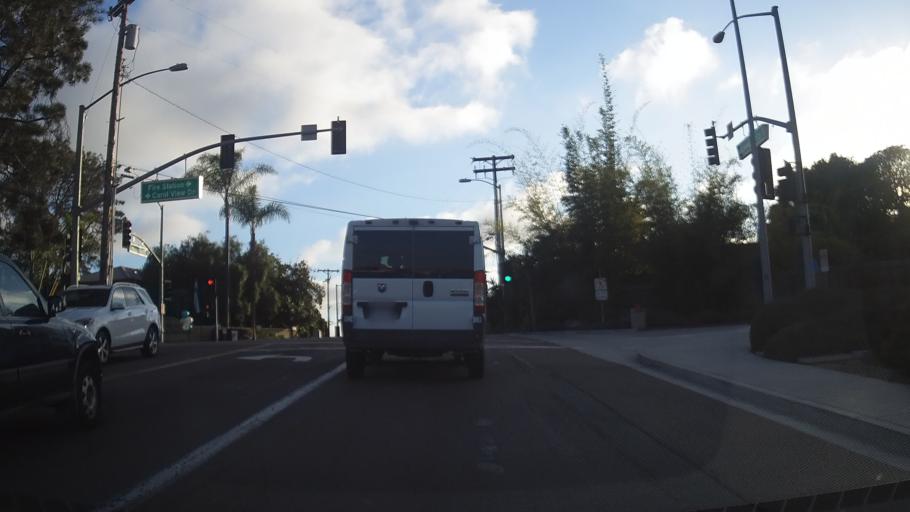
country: US
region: California
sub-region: San Diego County
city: Encinitas
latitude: 33.0261
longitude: -117.2765
